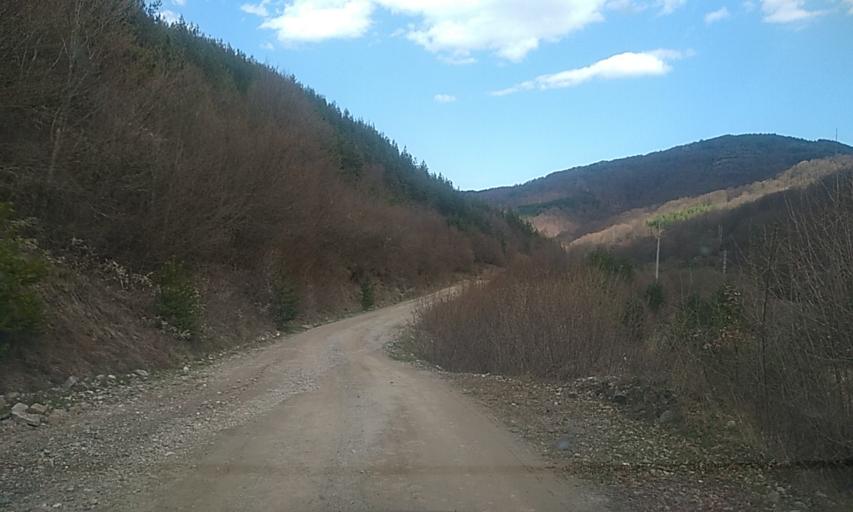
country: MK
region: Kriva Palanka
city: Kriva Palanka
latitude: 42.3409
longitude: 22.3778
